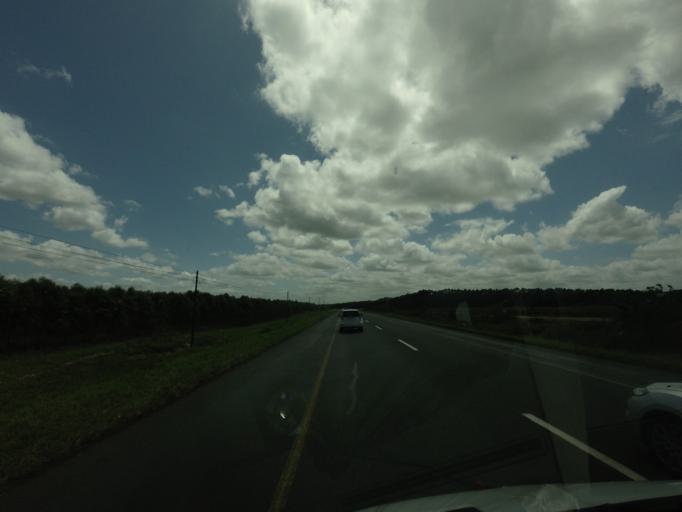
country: ZA
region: KwaZulu-Natal
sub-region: uThungulu District Municipality
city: KwaMbonambi
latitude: -28.5712
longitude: 32.1098
